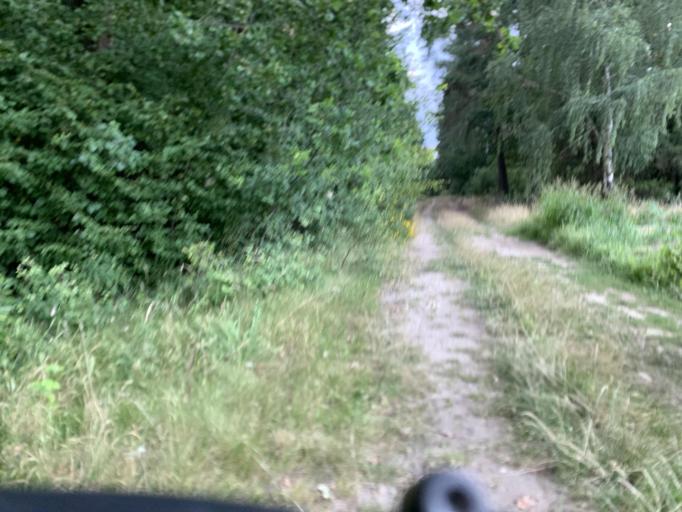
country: DE
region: Lower Saxony
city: Thomasburg
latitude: 53.2112
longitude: 10.6429
